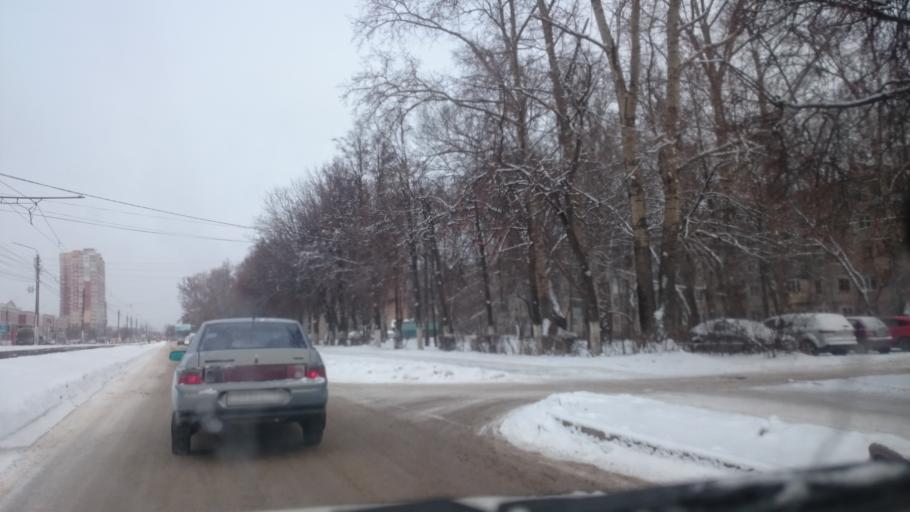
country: RU
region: Tula
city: Mendeleyevskiy
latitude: 54.1494
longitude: 37.5835
